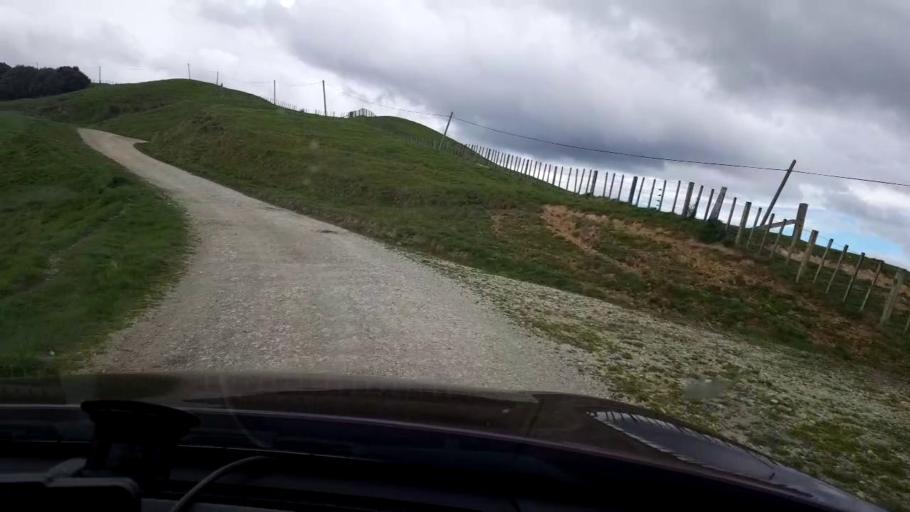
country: NZ
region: Gisborne
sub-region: Gisborne District
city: Gisborne
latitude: -38.3674
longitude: 177.9576
